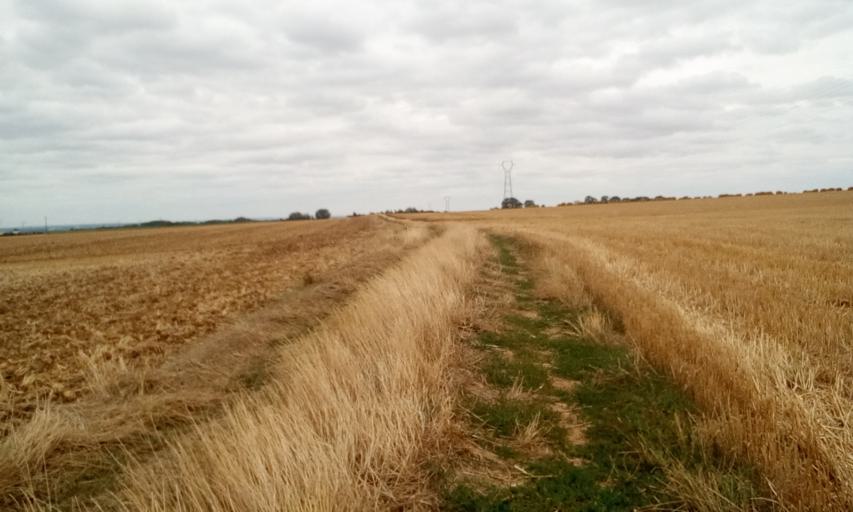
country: FR
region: Lower Normandy
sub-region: Departement du Calvados
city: Fontaine-Etoupefour
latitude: 49.1351
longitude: -0.4606
